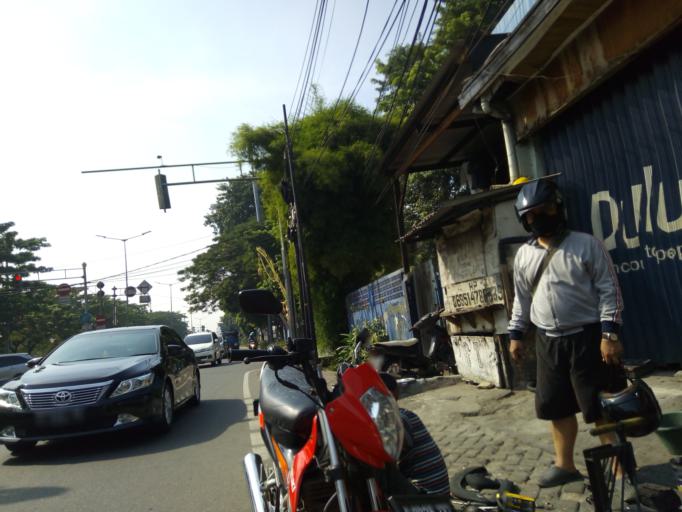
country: ID
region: Jakarta Raya
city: Jakarta
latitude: -6.2064
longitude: 106.8381
